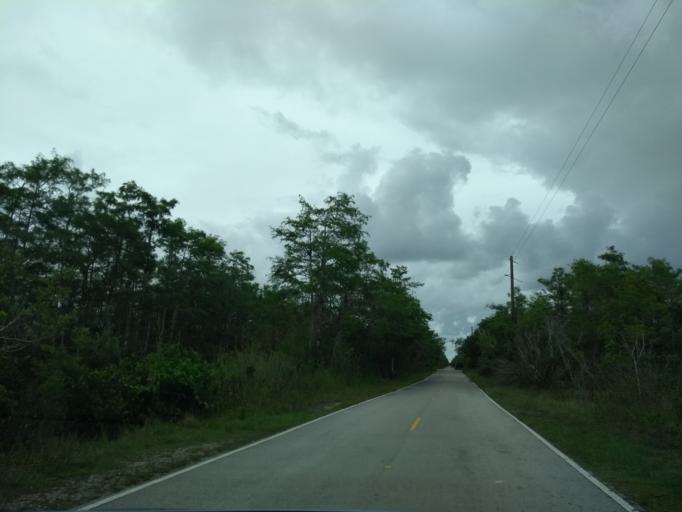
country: US
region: Florida
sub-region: Miami-Dade County
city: The Hammocks
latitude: 25.7613
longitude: -80.8996
